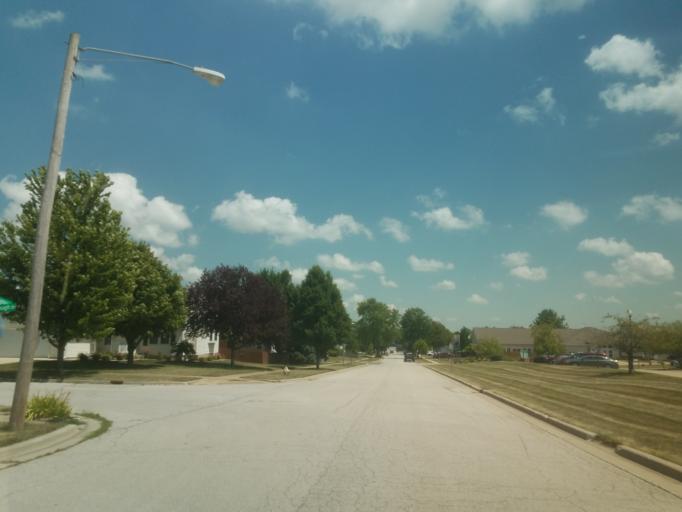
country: US
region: Illinois
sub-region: McLean County
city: Bloomington
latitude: 40.4424
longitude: -89.0343
